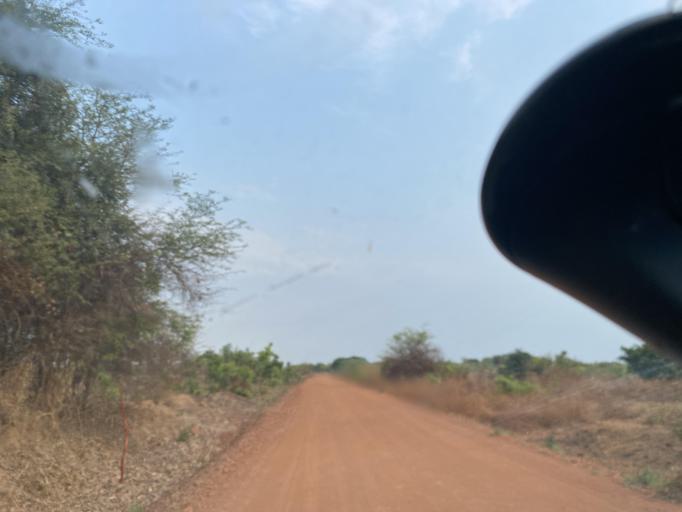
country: ZM
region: Lusaka
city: Chongwe
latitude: -15.2387
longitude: 28.5963
